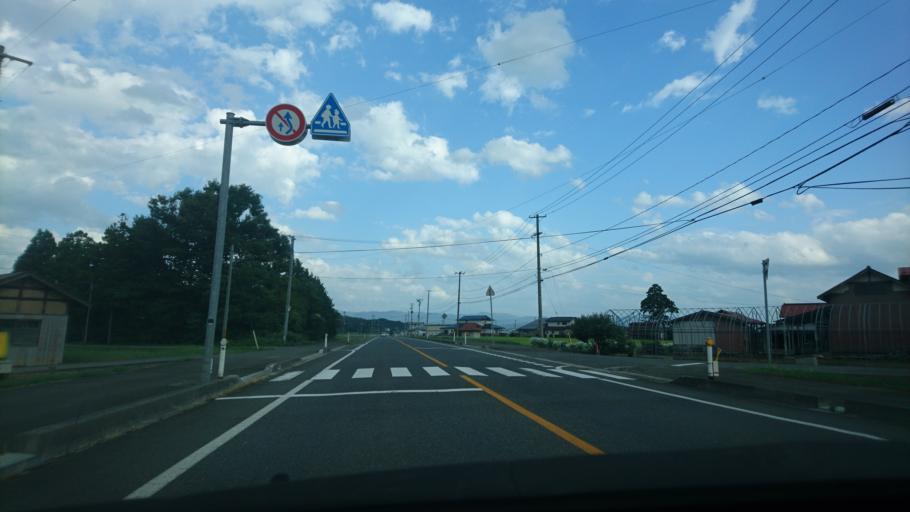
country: JP
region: Iwate
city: Kitakami
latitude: 39.2112
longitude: 141.1489
